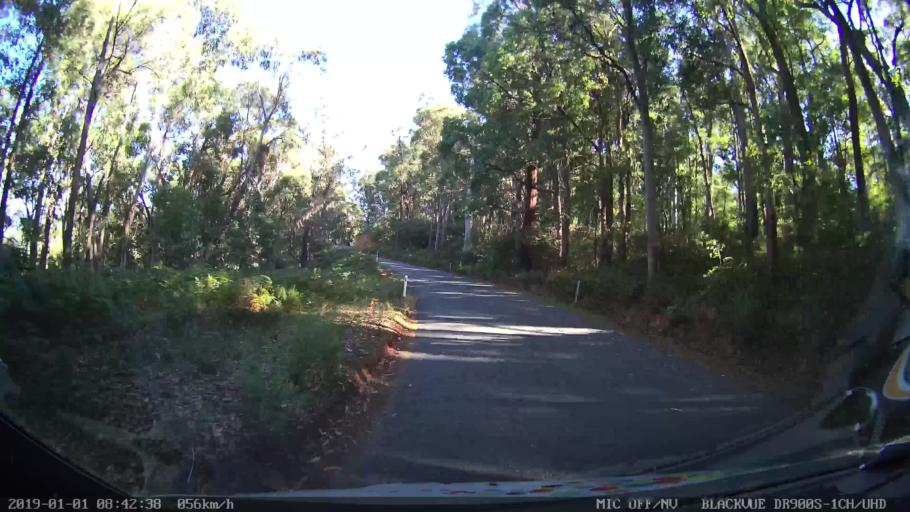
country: AU
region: New South Wales
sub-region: Snowy River
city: Jindabyne
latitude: -36.3223
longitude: 148.1927
